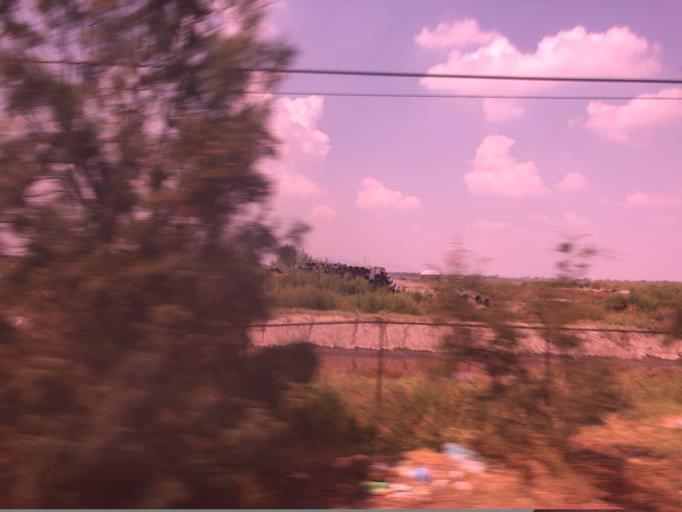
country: MX
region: Mexico
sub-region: Ciudad Nezahualcoyotl
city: Colonia Gustavo Baz Prada
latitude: 19.4633
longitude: -99.0217
